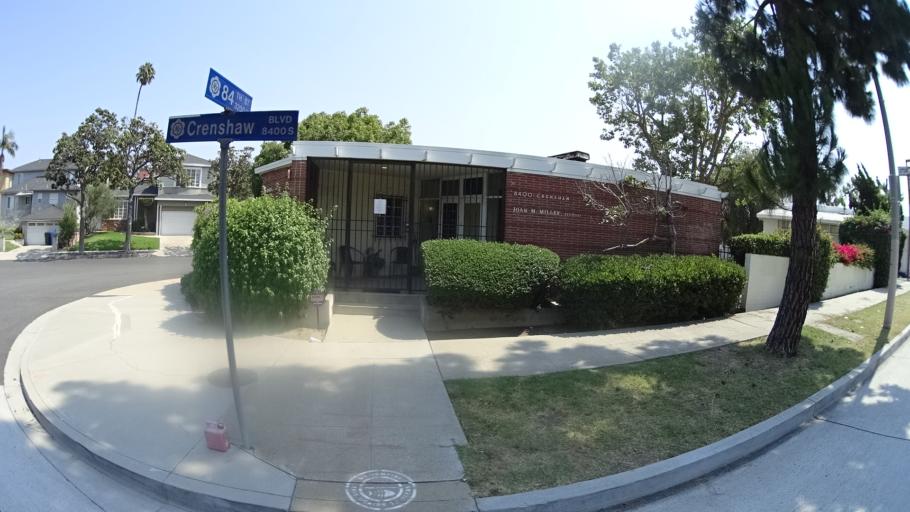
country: US
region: California
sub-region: Los Angeles County
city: Inglewood
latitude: 33.9627
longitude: -118.3283
